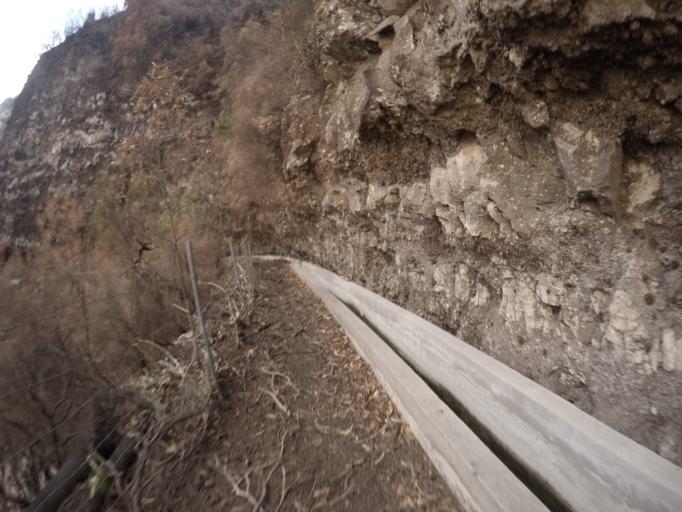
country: PT
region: Madeira
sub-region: Funchal
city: Nossa Senhora do Monte
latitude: 32.6897
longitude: -16.9160
